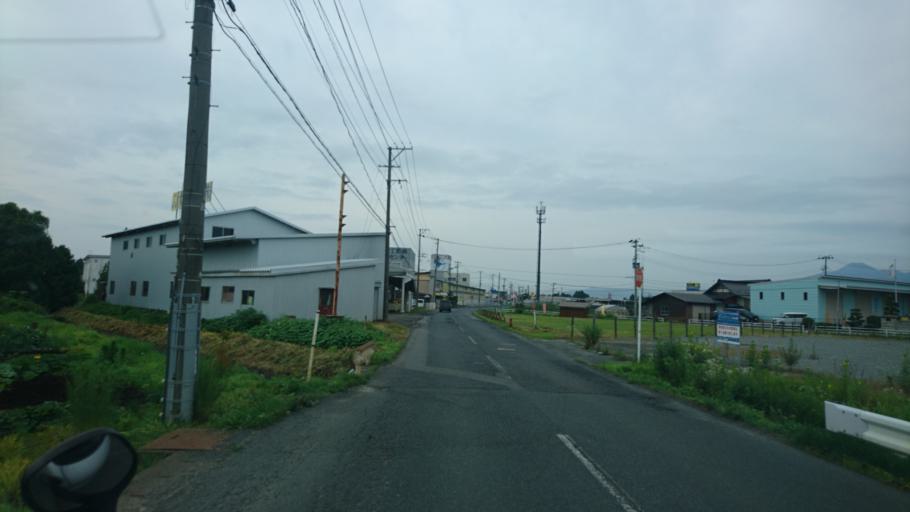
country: JP
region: Iwate
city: Morioka-shi
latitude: 39.6602
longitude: 141.1415
